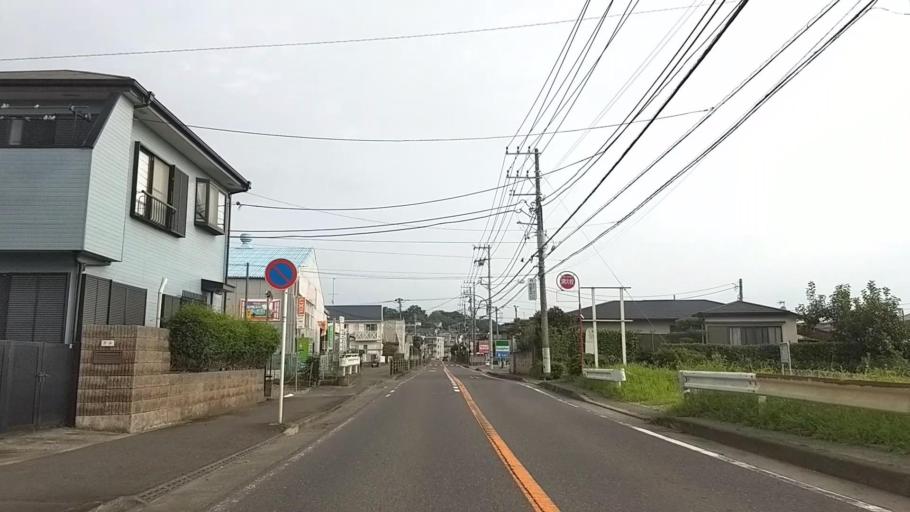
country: JP
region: Kanagawa
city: Isehara
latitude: 35.3499
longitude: 139.3024
